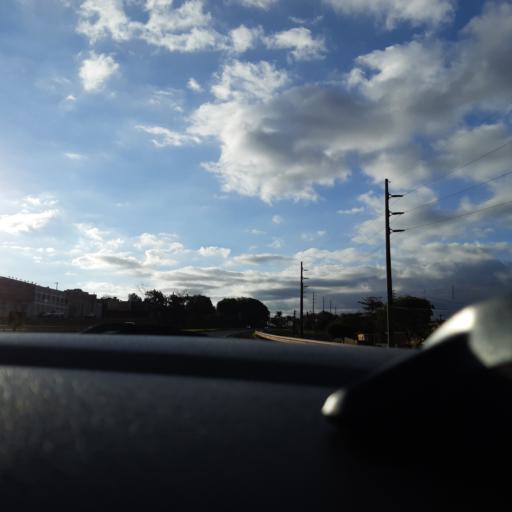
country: BR
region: Sao Paulo
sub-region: Ourinhos
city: Ourinhos
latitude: -22.9887
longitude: -49.8541
